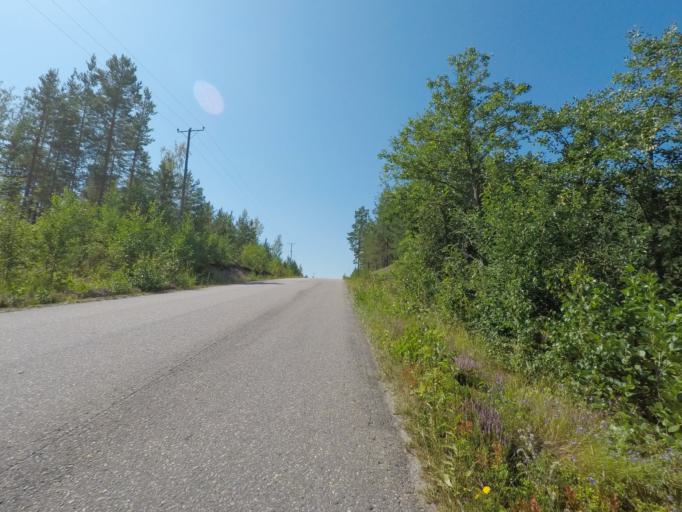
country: FI
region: Southern Savonia
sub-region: Mikkeli
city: Puumala
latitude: 61.4298
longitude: 28.1679
